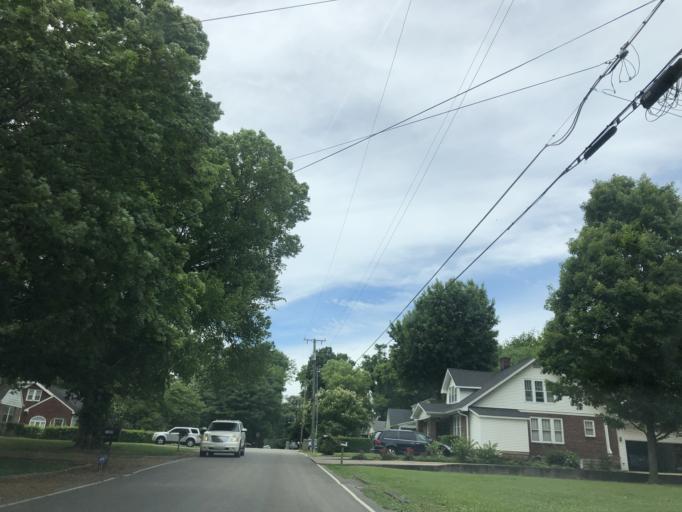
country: US
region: Tennessee
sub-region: Davidson County
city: Oak Hill
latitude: 36.1053
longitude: -86.7931
